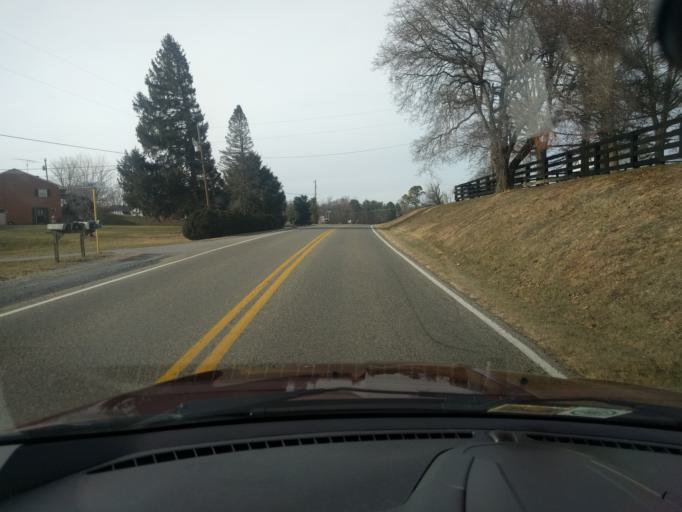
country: US
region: Virginia
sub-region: Augusta County
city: Stuarts Draft
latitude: 38.0353
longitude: -79.0703
